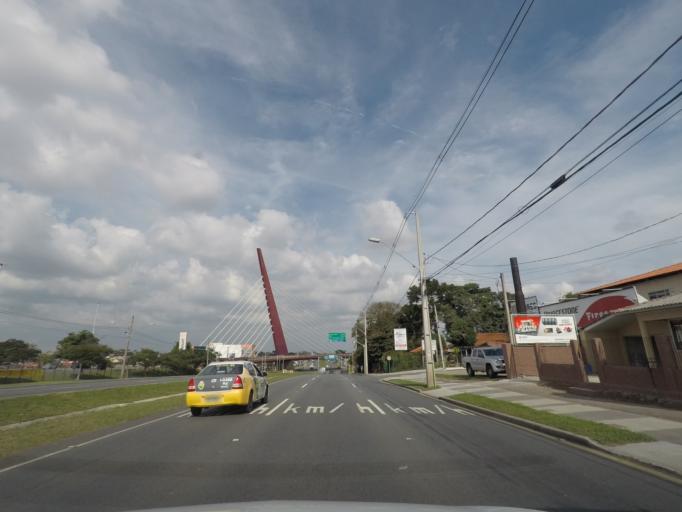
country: BR
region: Parana
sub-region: Pinhais
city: Pinhais
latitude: -25.4631
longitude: -49.2360
